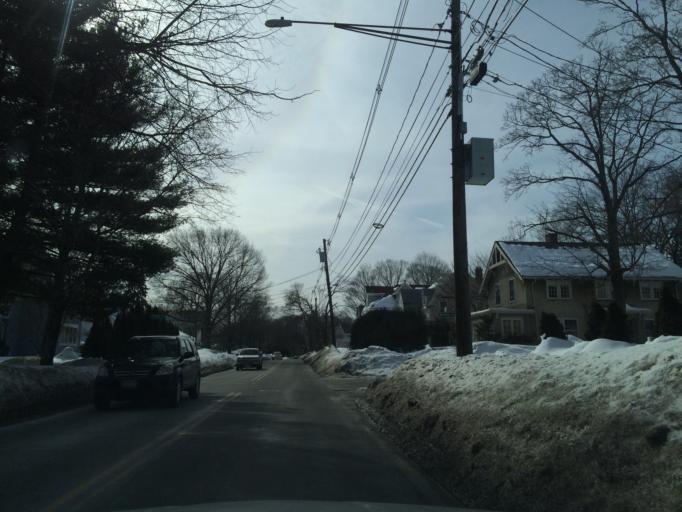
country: US
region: Massachusetts
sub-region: Middlesex County
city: Newton
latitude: 42.3610
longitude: -71.2104
